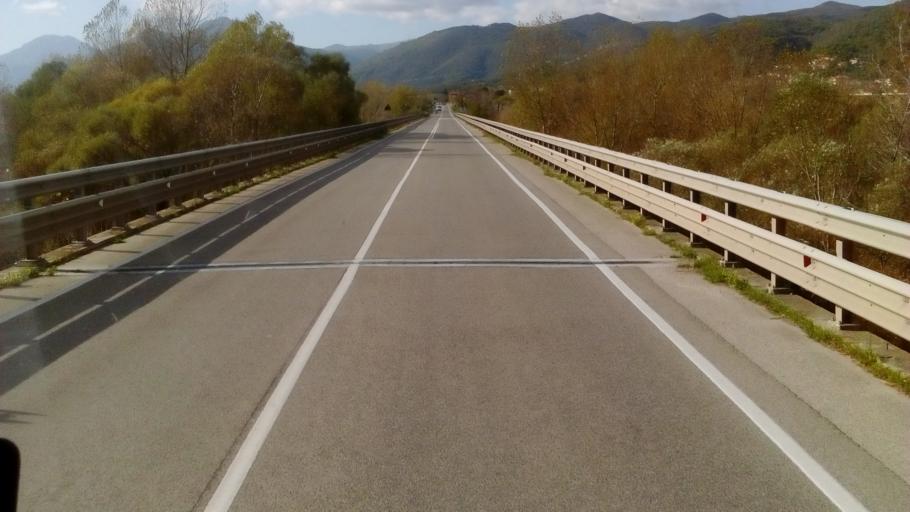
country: IT
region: Molise
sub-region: Provincia di Isernia
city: Taverna Ravindola
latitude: 41.5182
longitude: 14.1377
